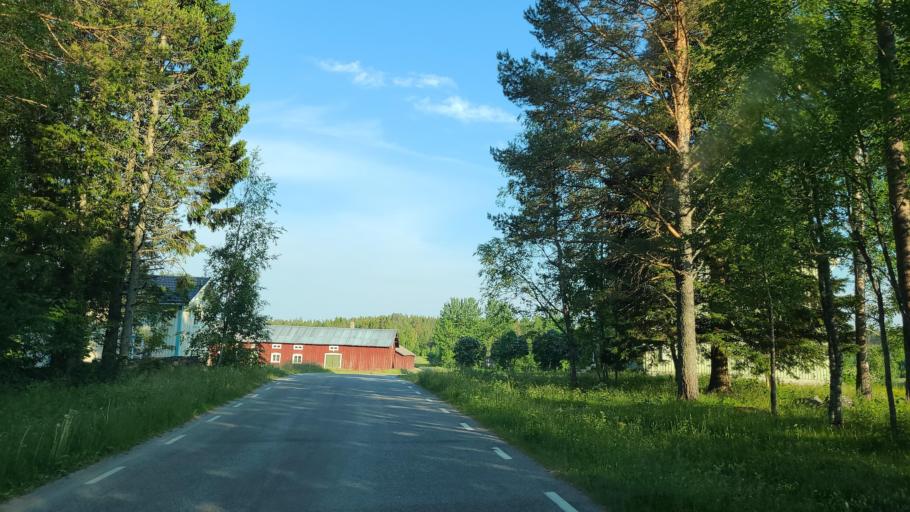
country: SE
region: Vaesterbotten
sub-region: Skelleftea Kommun
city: Burea
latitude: 64.3450
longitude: 21.3408
